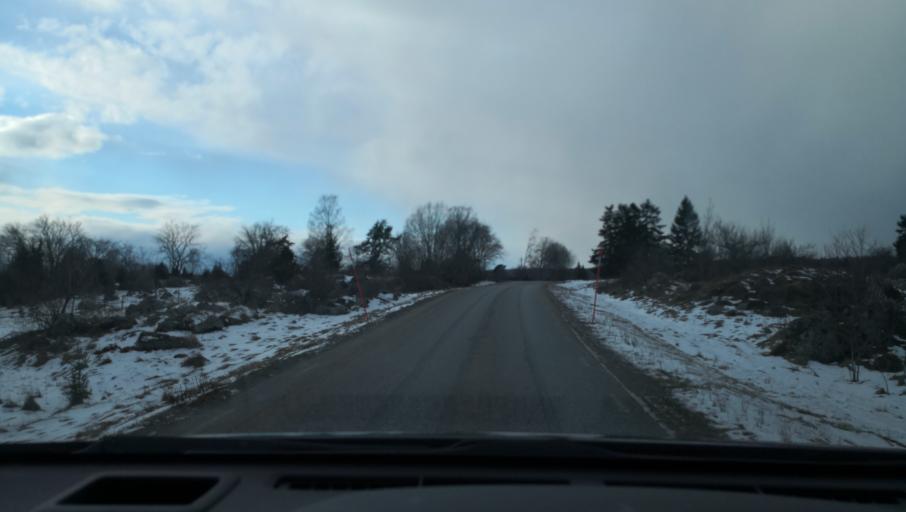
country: SE
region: Uppsala
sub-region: Enkopings Kommun
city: Irsta
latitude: 59.7032
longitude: 16.9257
